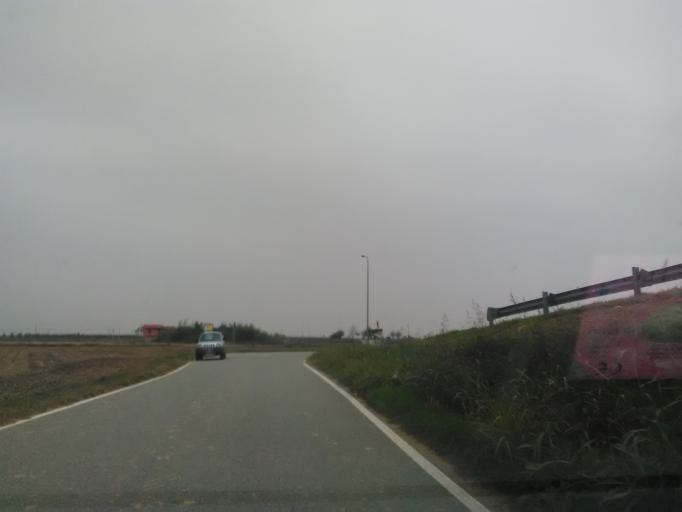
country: IT
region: Piedmont
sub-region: Provincia di Vercelli
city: Bianze
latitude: 45.3075
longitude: 8.1096
